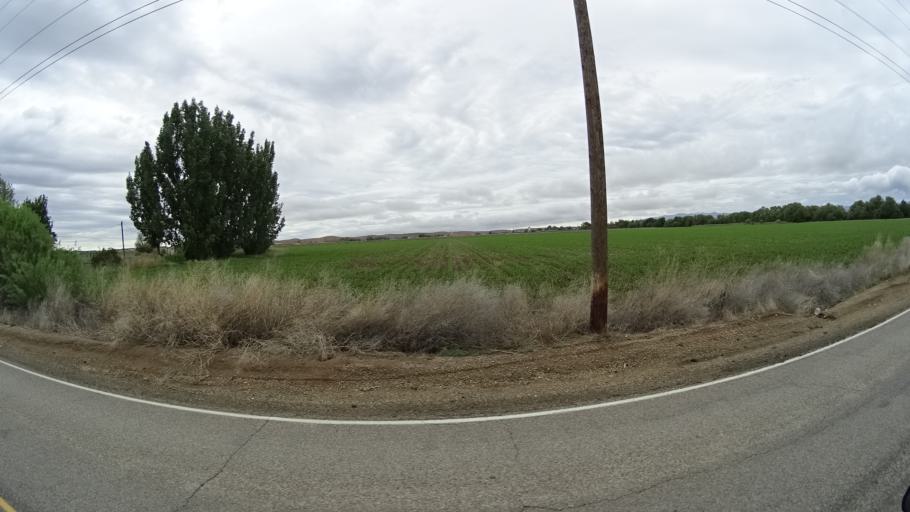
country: US
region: Idaho
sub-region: Ada County
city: Star
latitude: 43.7076
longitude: -116.4385
